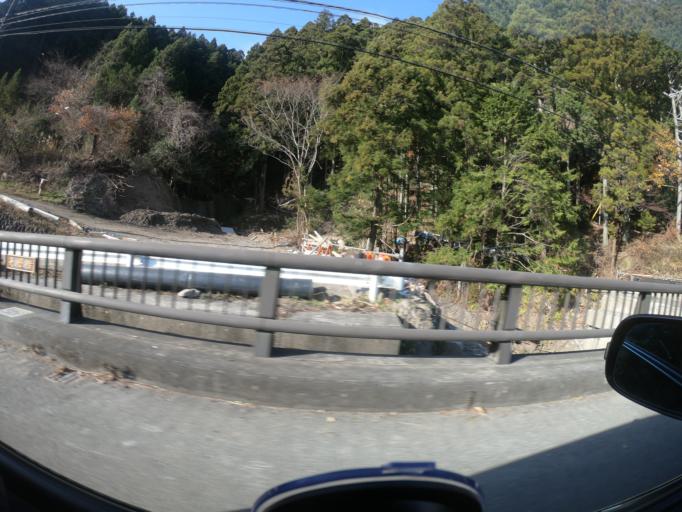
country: JP
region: Shizuoka
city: Kanaya
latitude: 35.0577
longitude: 138.0875
